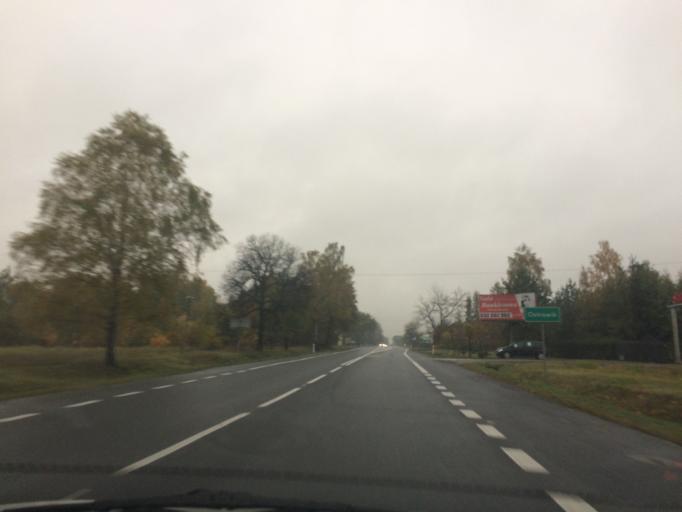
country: PL
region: Masovian Voivodeship
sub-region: Powiat otwocki
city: Celestynow
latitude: 52.0951
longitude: 21.4120
